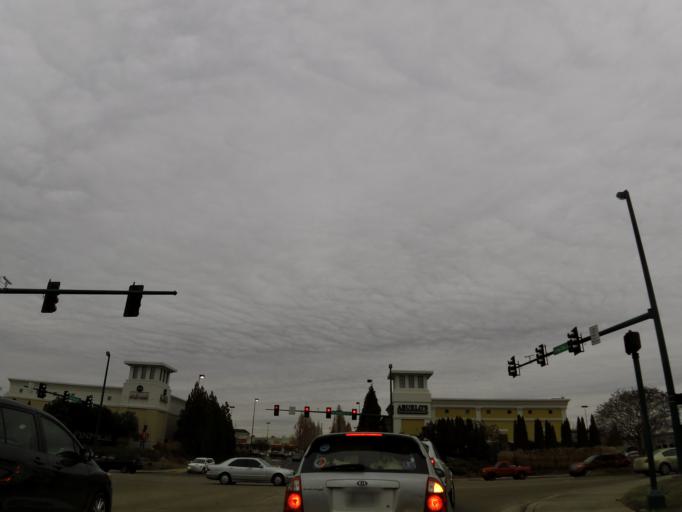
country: US
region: Tennessee
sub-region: Knox County
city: Farragut
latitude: 35.8997
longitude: -84.1580
